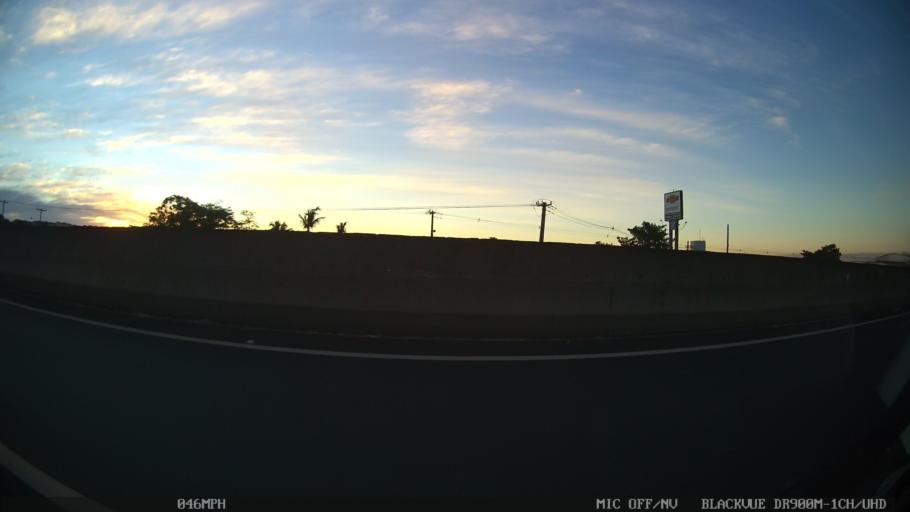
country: BR
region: Sao Paulo
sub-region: Catanduva
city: Catanduva
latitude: -21.1291
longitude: -49.0095
